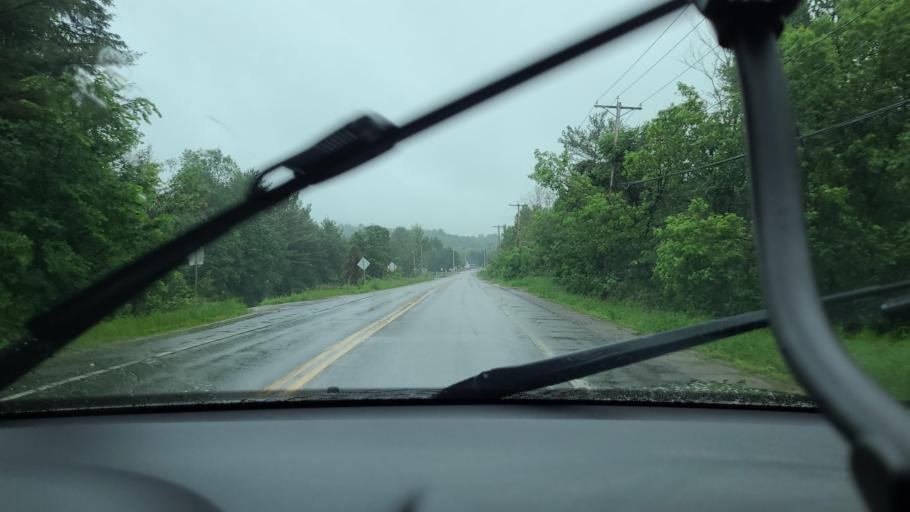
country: CA
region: Quebec
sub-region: Outaouais
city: Papineauville
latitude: 45.6726
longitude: -75.0217
